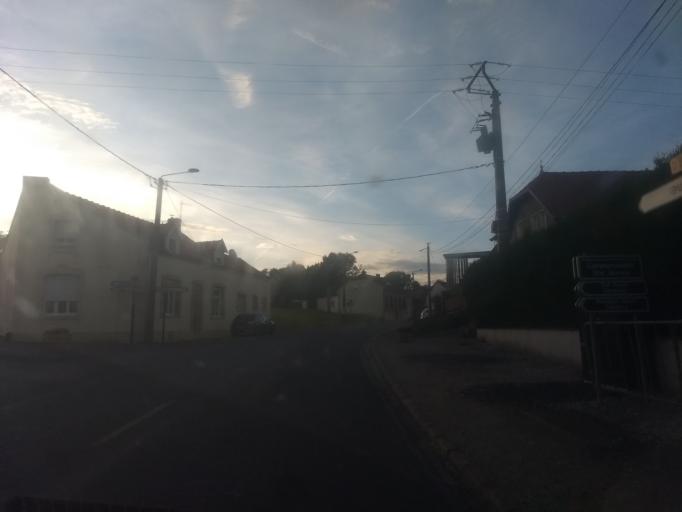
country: FR
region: Nord-Pas-de-Calais
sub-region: Departement du Pas-de-Calais
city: Bucquoy
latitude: 50.1186
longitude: 2.6920
